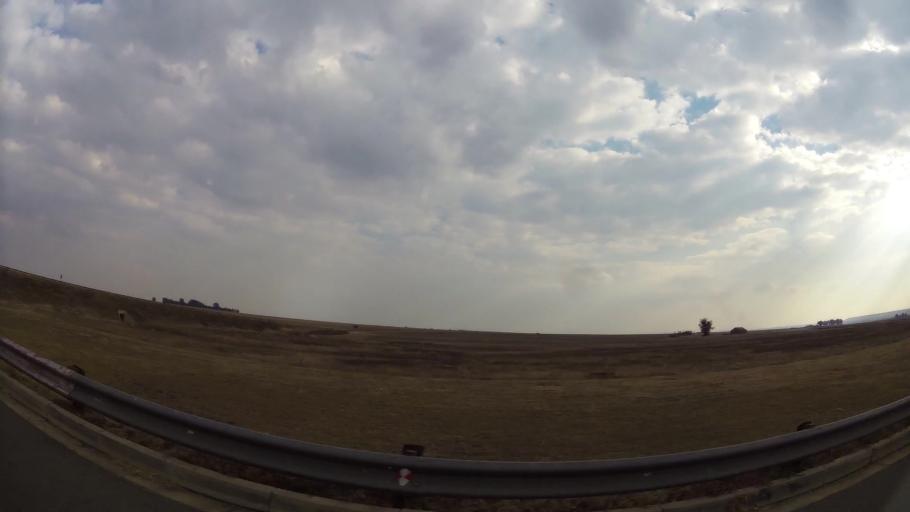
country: ZA
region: Gauteng
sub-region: Ekurhuleni Metropolitan Municipality
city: Nigel
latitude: -26.3191
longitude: 28.5893
